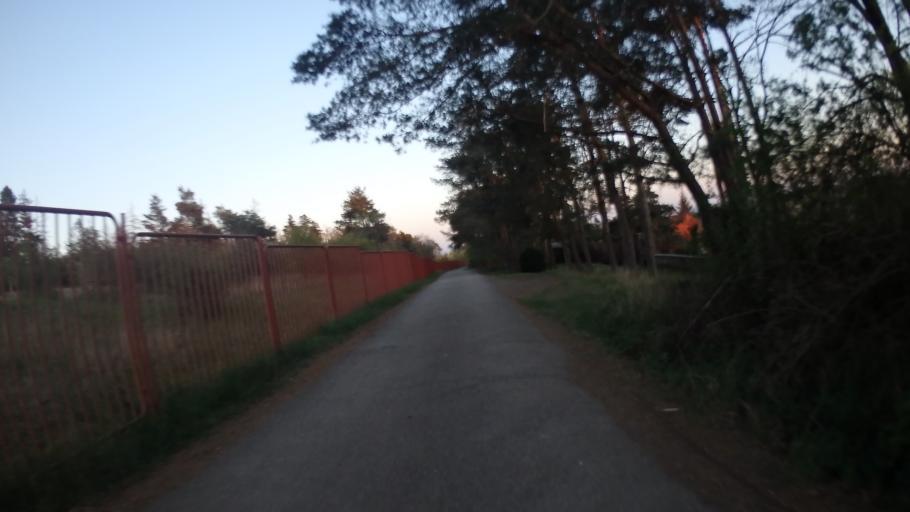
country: CZ
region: South Moravian
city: Ostopovice
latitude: 49.1830
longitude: 16.5515
